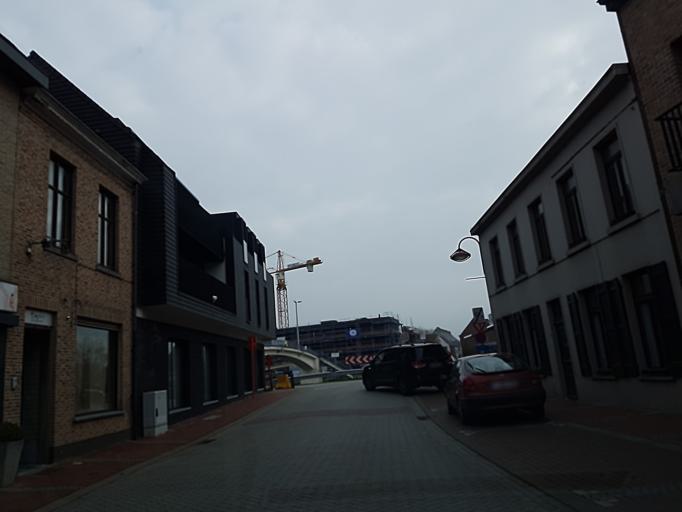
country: BE
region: Flanders
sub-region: Provincie Oost-Vlaanderen
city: Nevele
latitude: 51.0326
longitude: 3.5499
